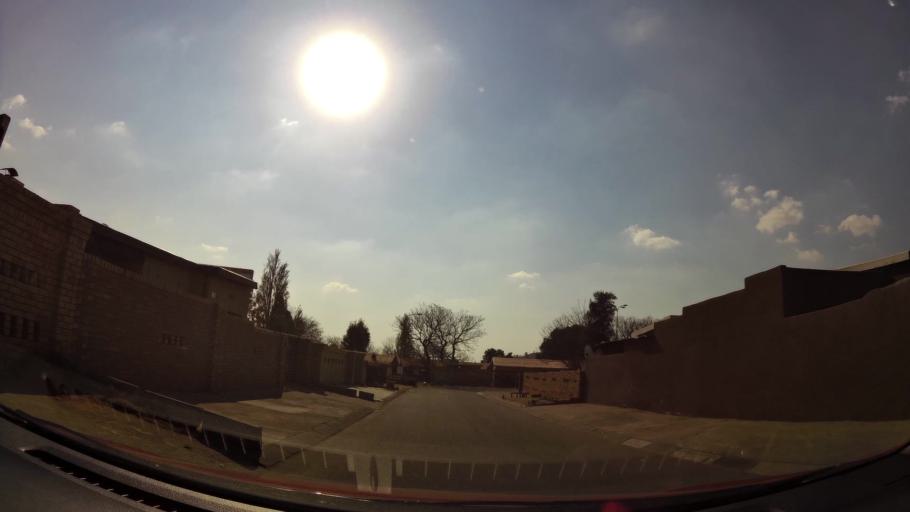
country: ZA
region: Gauteng
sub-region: City of Johannesburg Metropolitan Municipality
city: Soweto
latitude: -26.2391
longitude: 27.9478
